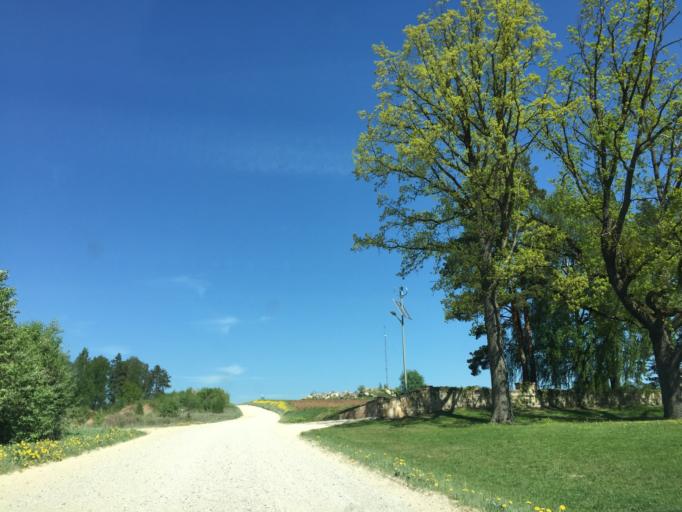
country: LV
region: Ikskile
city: Ikskile
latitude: 56.8639
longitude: 24.5019
